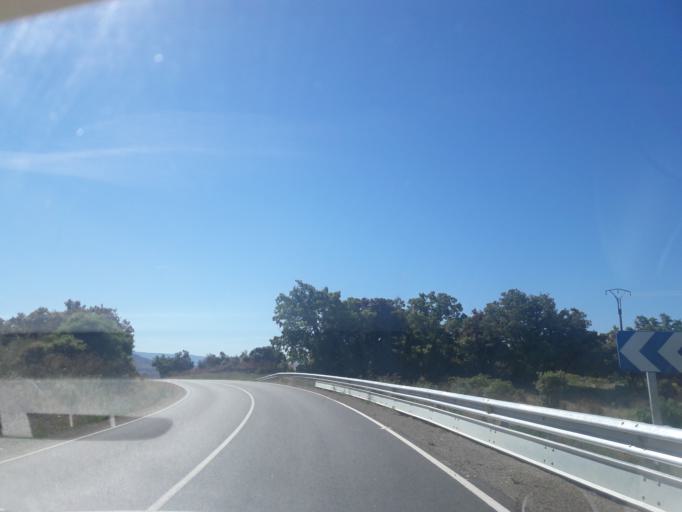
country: ES
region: Castille and Leon
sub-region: Provincia de Salamanca
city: Nava de Bejar
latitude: 40.4852
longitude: -5.6525
